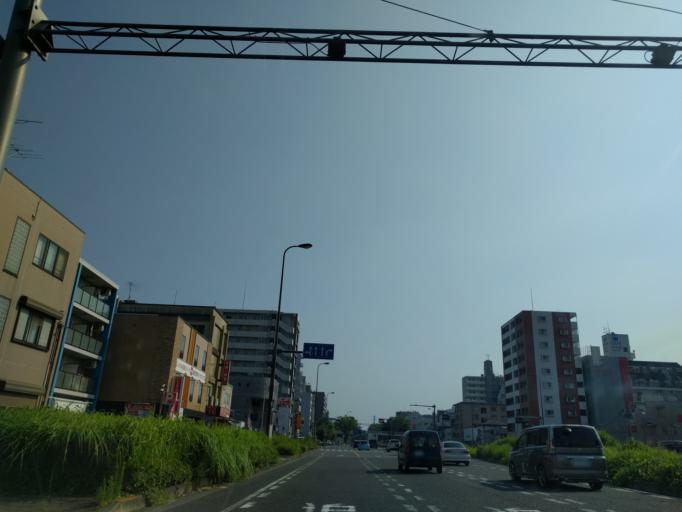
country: JP
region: Kanagawa
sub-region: Kawasaki-shi
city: Kawasaki
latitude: 35.5185
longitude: 139.6892
